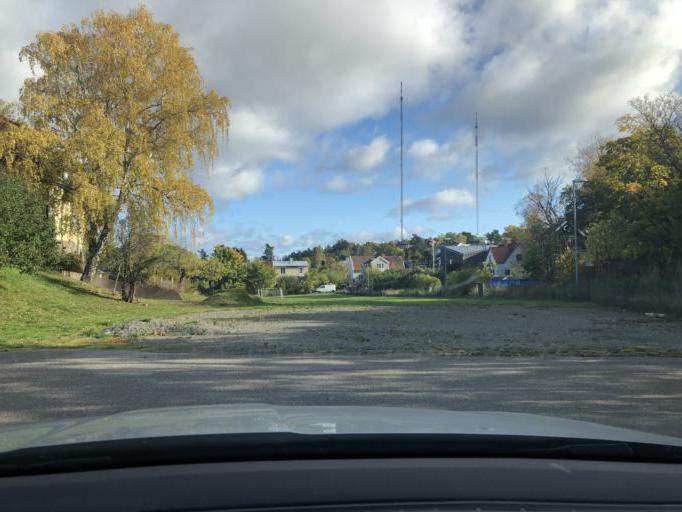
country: SE
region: Stockholm
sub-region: Nacka Kommun
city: Nacka
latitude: 59.2983
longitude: 18.1563
